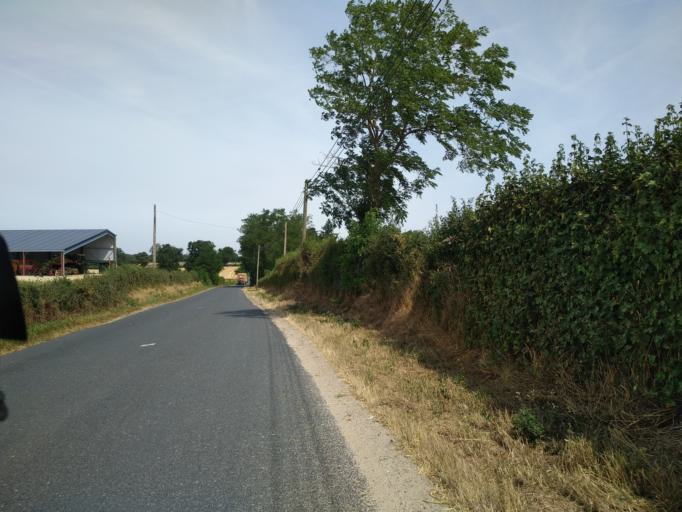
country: FR
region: Auvergne
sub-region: Departement de l'Allier
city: Molinet
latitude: 46.4254
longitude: 3.9762
